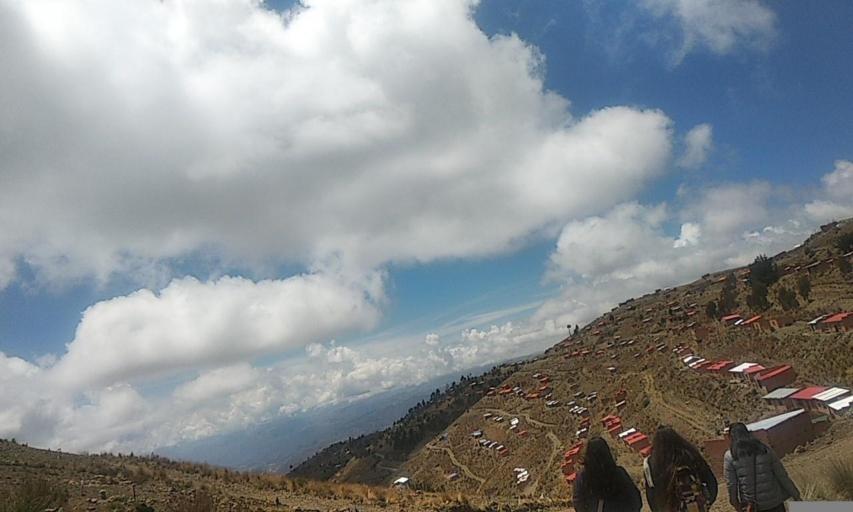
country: BO
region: La Paz
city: La Paz
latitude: -16.4616
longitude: -68.1365
